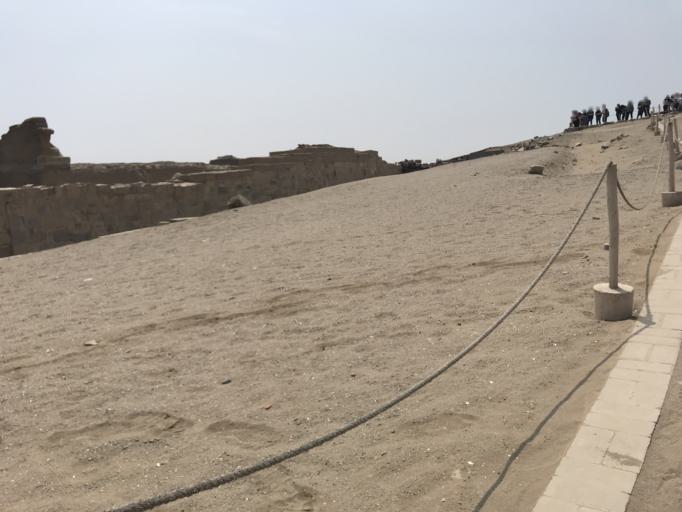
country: PE
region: Lima
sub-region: Lima
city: Punta Hermosa
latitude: -12.2548
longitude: -76.8965
